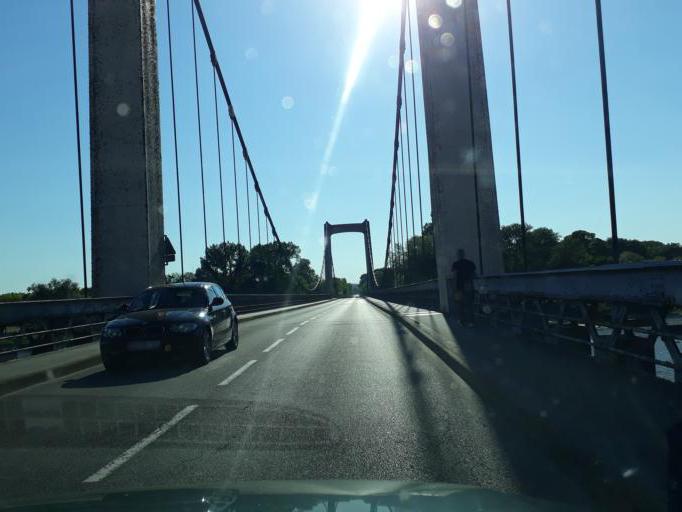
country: FR
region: Bourgogne
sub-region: Departement de la Nievre
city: Cosne-Cours-sur-Loire
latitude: 47.4115
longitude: 2.9212
